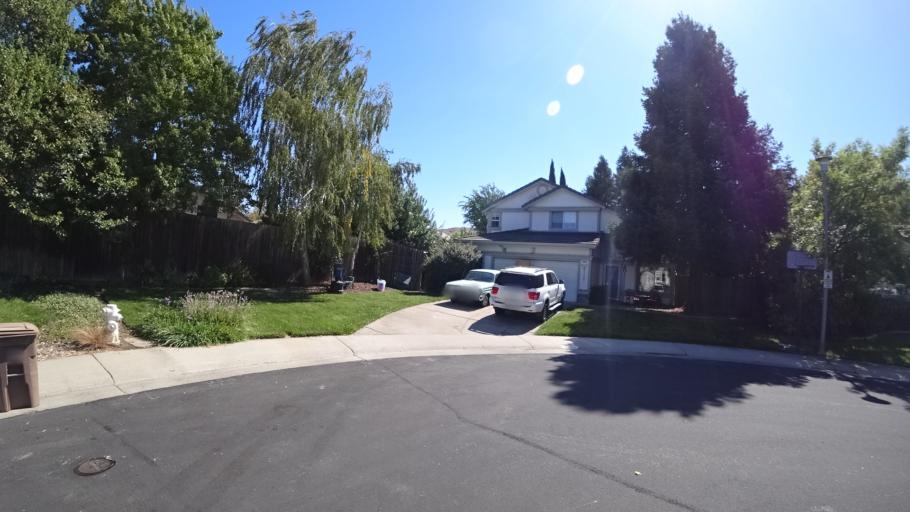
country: US
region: California
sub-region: Sacramento County
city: Laguna
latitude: 38.4346
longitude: -121.4272
